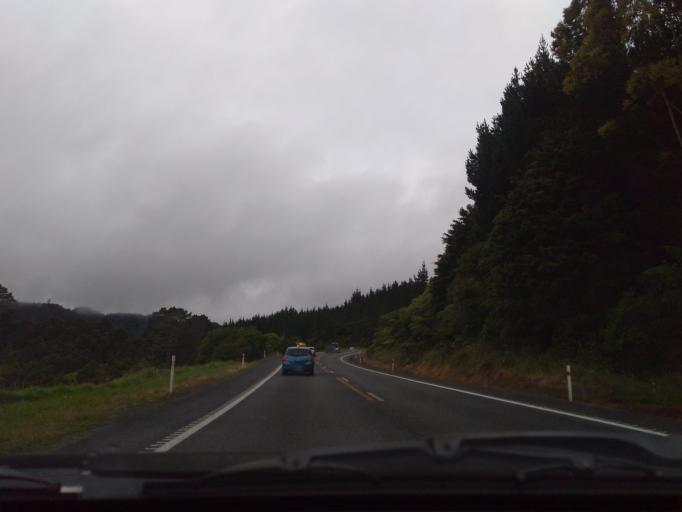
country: NZ
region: Northland
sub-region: Whangarei
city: Ruakaka
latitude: -36.0896
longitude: 174.4305
